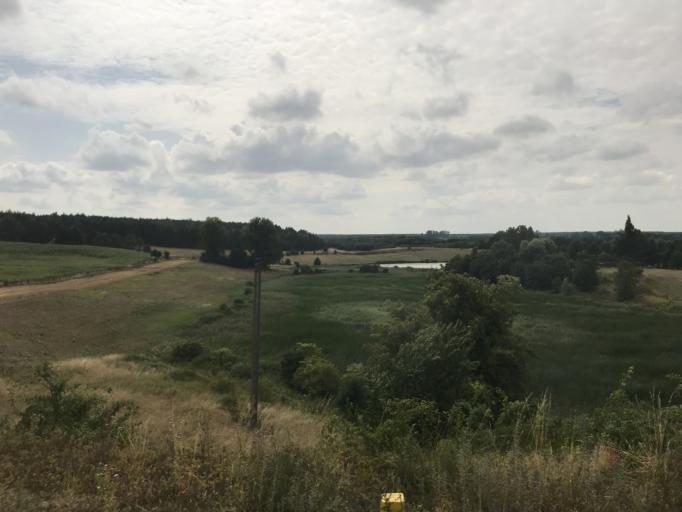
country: PL
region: Greater Poland Voivodeship
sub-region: Powiat gnieznienski
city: Niechanowo
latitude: 52.5380
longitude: 17.7171
